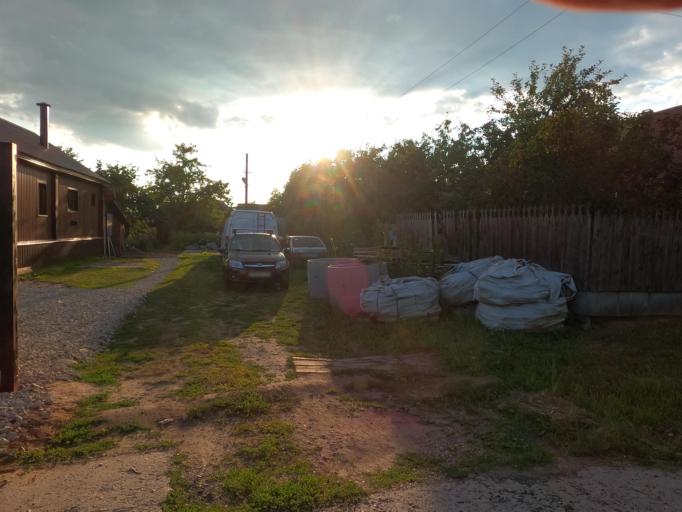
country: RU
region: Moskovskaya
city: Ashitkovo
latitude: 55.4170
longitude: 38.5796
